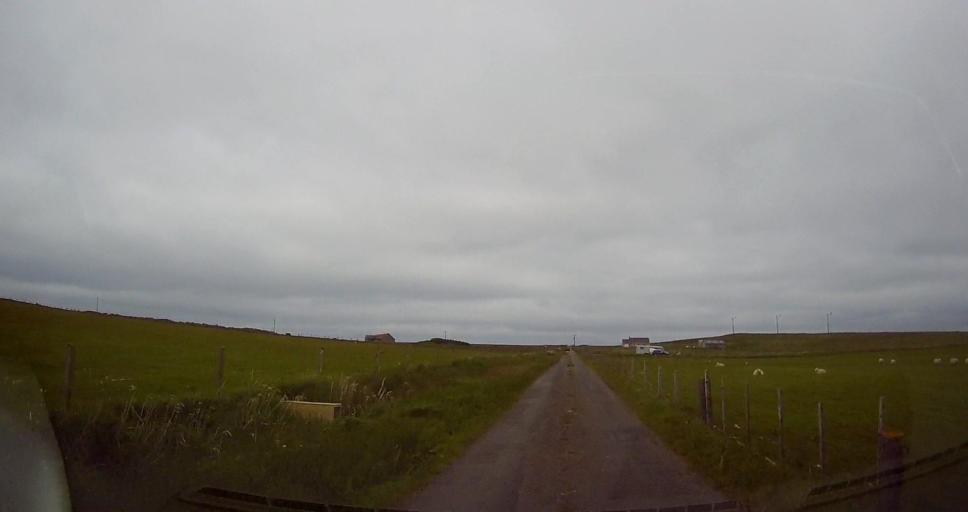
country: GB
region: Scotland
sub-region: Orkney Islands
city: Kirkwall
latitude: 58.9545
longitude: -2.7152
